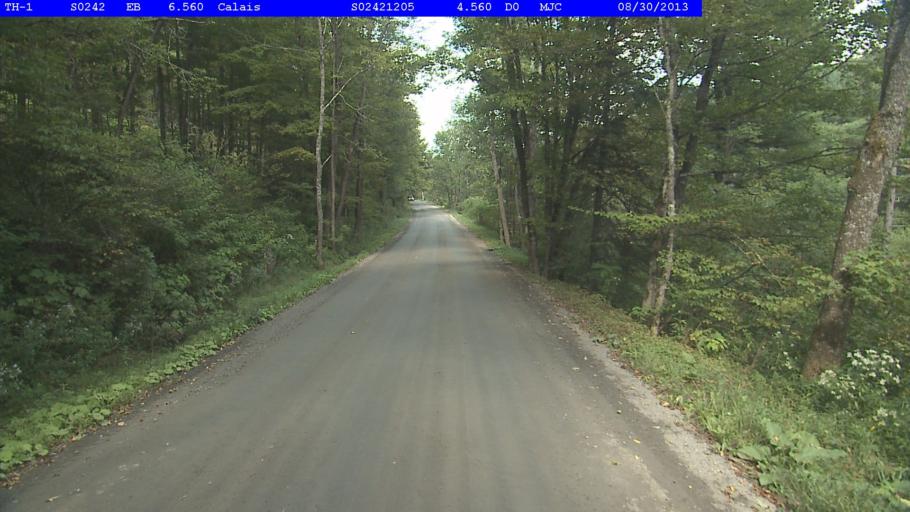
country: US
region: Vermont
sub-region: Washington County
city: Montpelier
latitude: 44.3720
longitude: -72.4615
